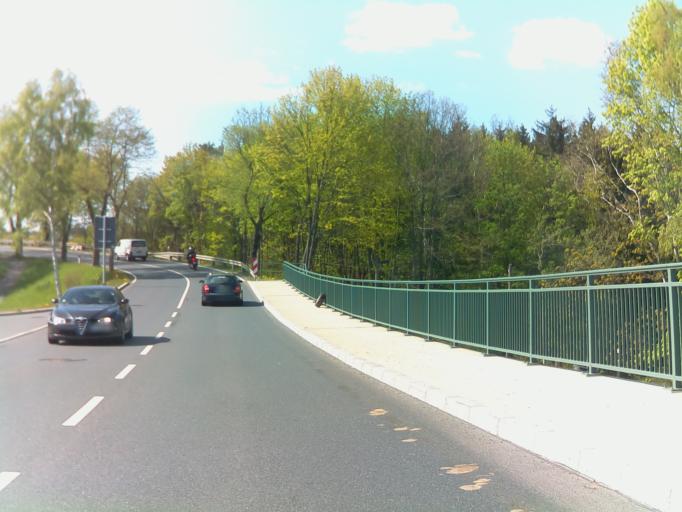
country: DE
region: Saxony
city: Mehltheuer
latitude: 50.5457
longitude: 12.0413
